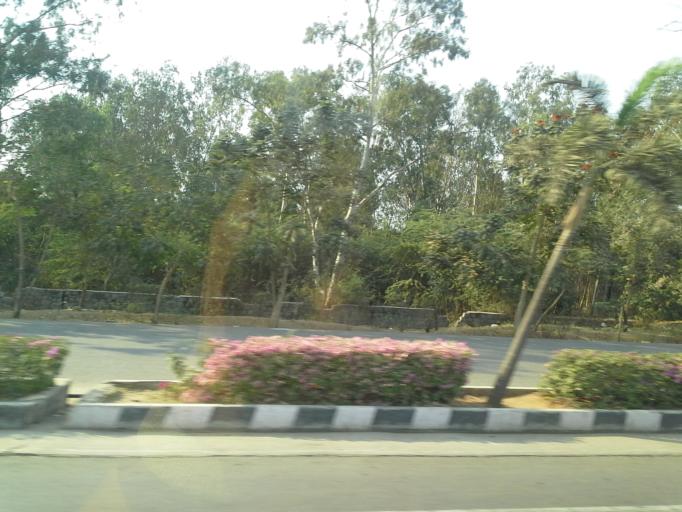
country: IN
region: Telangana
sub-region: Rangareddi
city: Balapur
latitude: 17.3128
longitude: 78.4241
